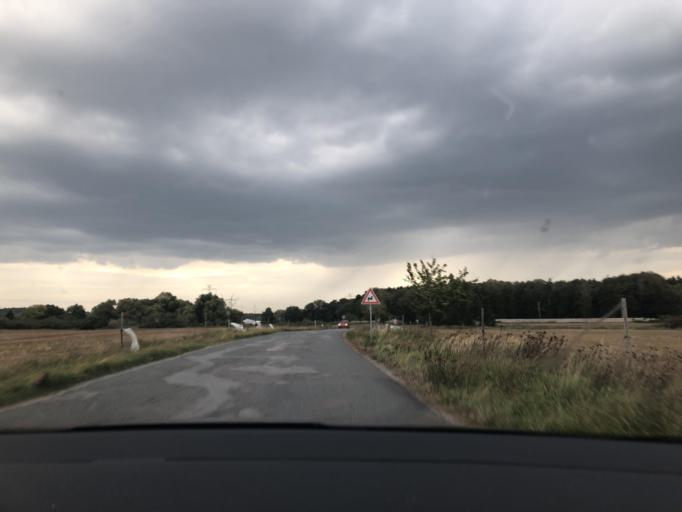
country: CZ
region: Pardubicky
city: Chvaletice
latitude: 50.0513
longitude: 15.4002
